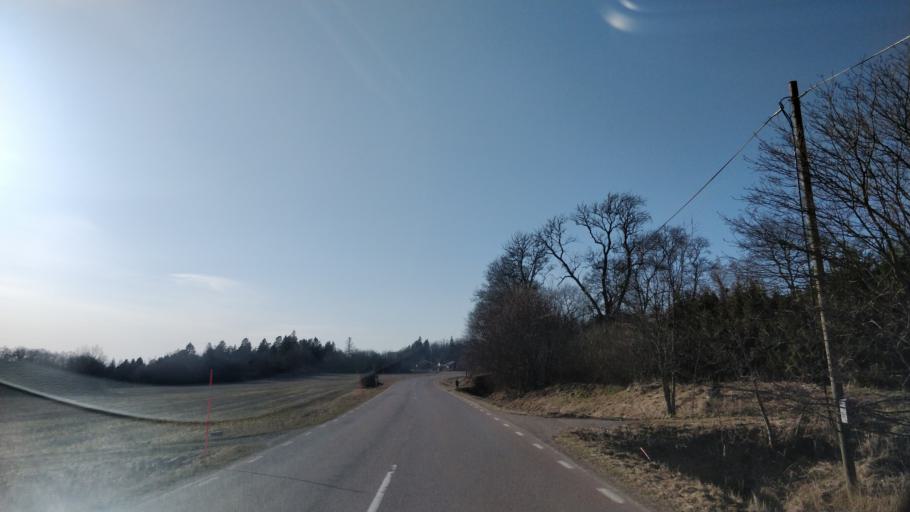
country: SE
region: Uppsala
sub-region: Enkopings Kommun
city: Orsundsbro
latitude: 59.7416
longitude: 17.2907
